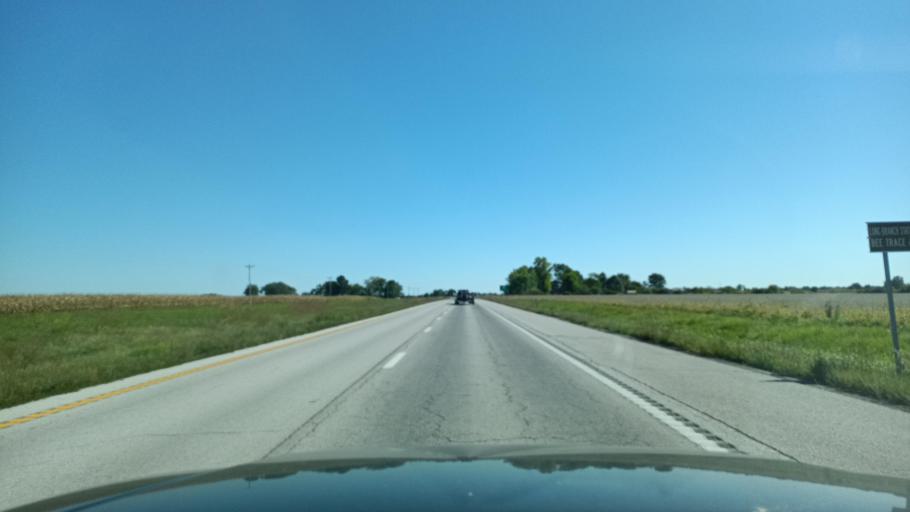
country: US
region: Missouri
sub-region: Macon County
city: Macon
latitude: 39.8290
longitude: -92.4745
